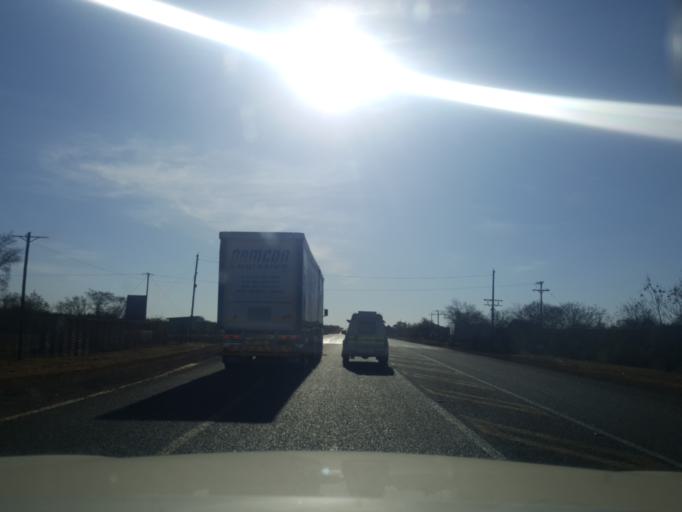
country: ZA
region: North-West
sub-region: Ngaka Modiri Molema District Municipality
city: Zeerust
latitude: -25.5318
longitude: 26.0218
